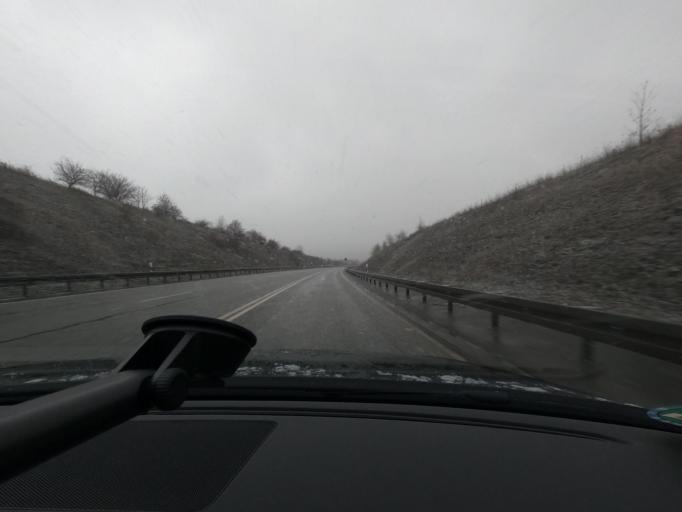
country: DE
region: Thuringia
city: Dingelstadt
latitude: 51.3257
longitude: 10.3285
